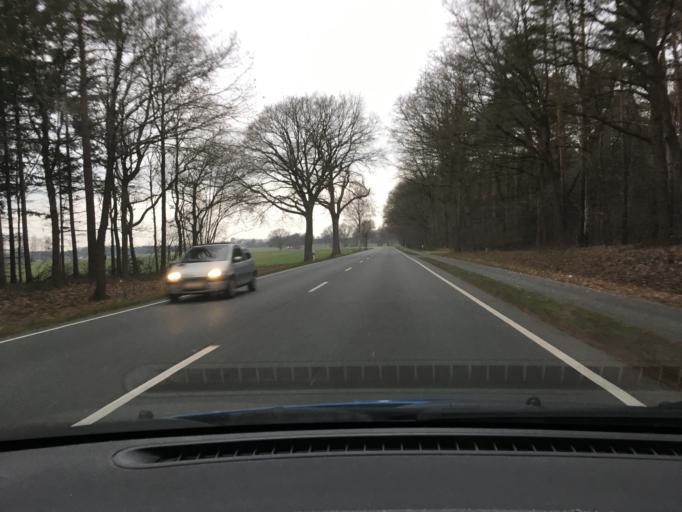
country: DE
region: Lower Saxony
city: Bad Fallingbostel
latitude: 52.8612
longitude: 9.6584
